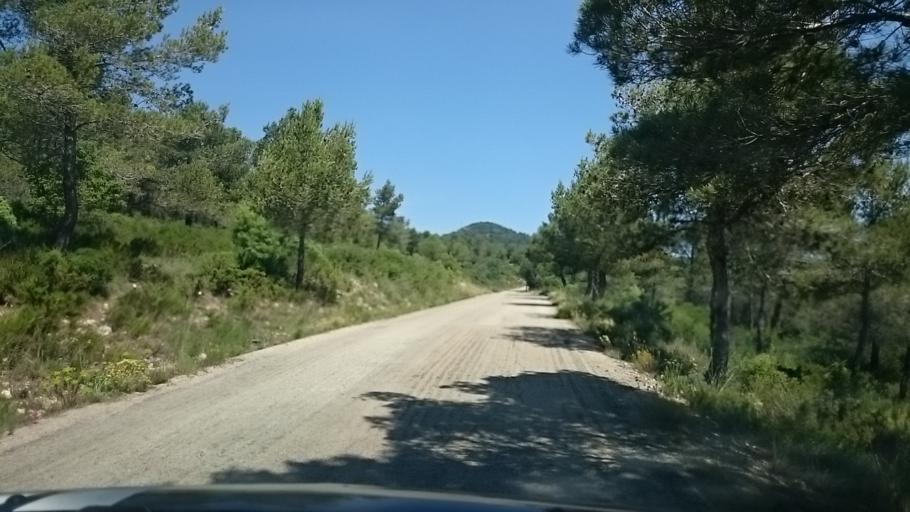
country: ES
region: Catalonia
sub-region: Provincia de Tarragona
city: Querol
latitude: 41.3948
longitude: 1.4268
